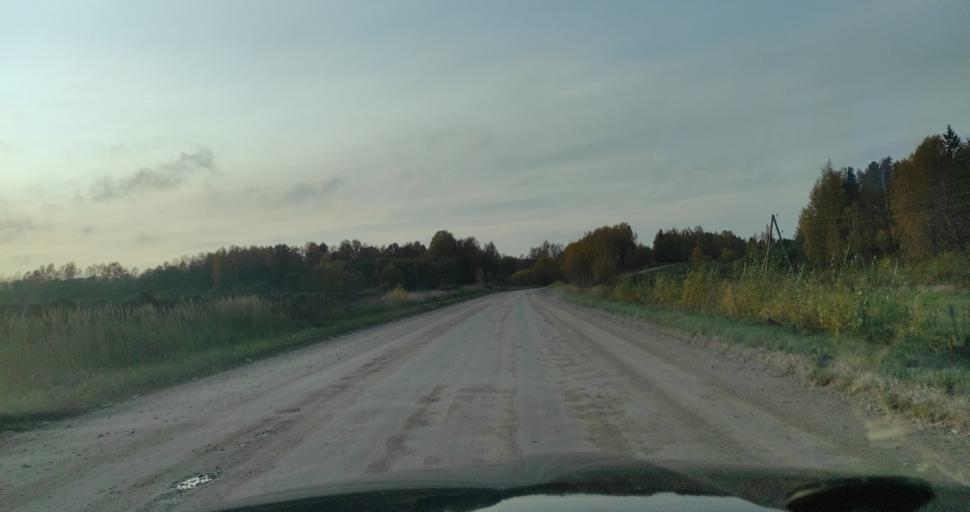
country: LV
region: Vainode
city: Vainode
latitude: 56.4901
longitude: 21.8460
